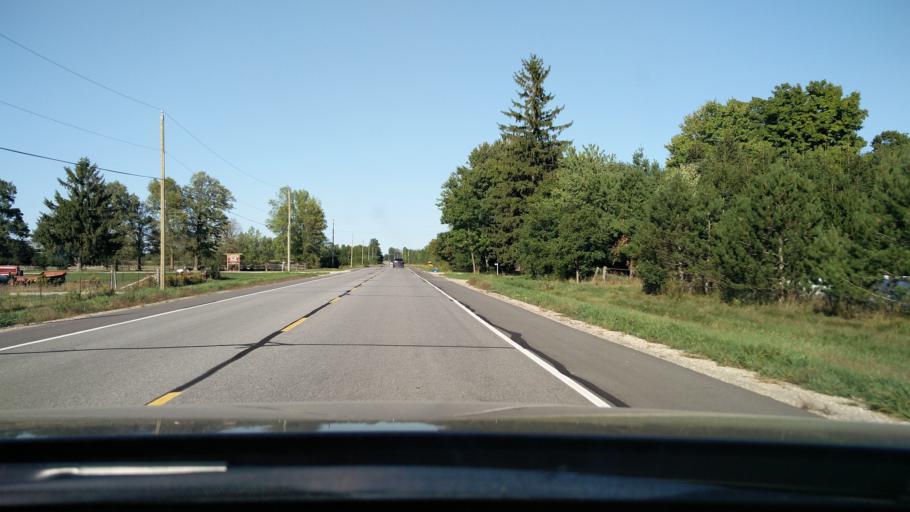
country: CA
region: Ontario
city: Perth
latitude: 44.9568
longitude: -76.1594
